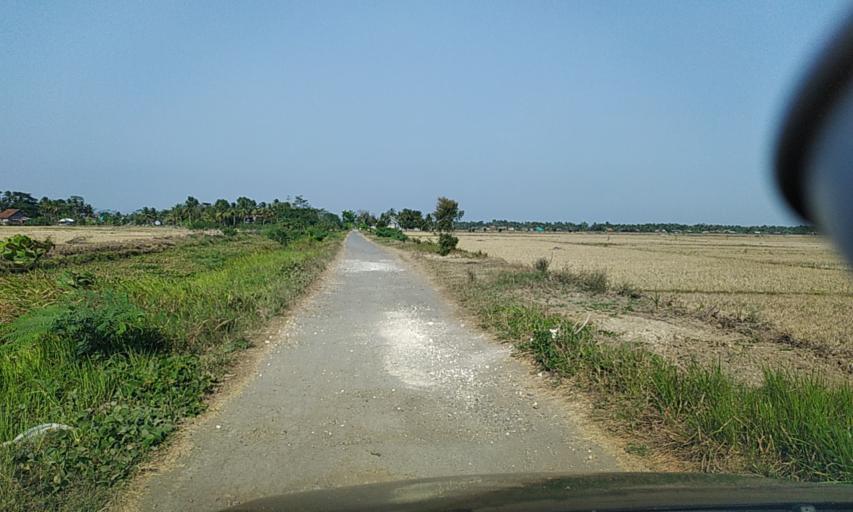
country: ID
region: Central Java
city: Pondokwungu
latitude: -7.5481
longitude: 108.8052
